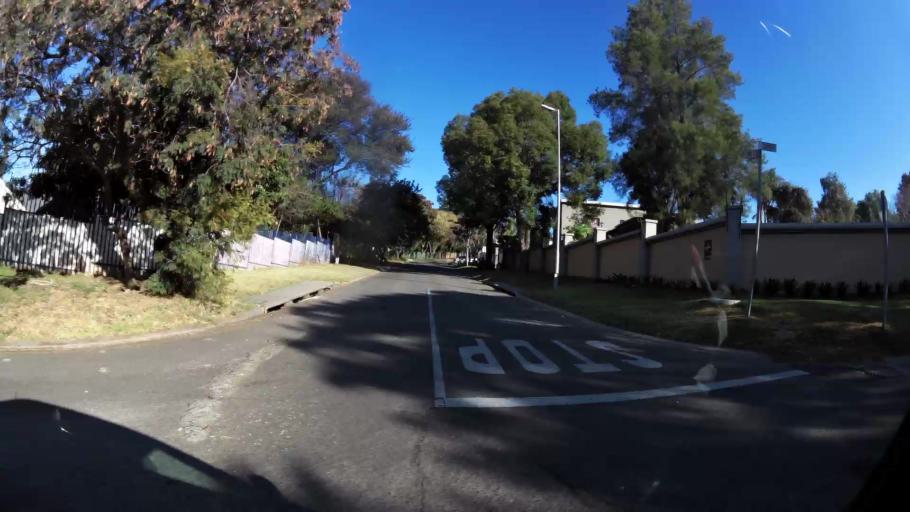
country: ZA
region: Gauteng
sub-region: City of Johannesburg Metropolitan Municipality
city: Midrand
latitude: -26.0321
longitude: 28.0463
